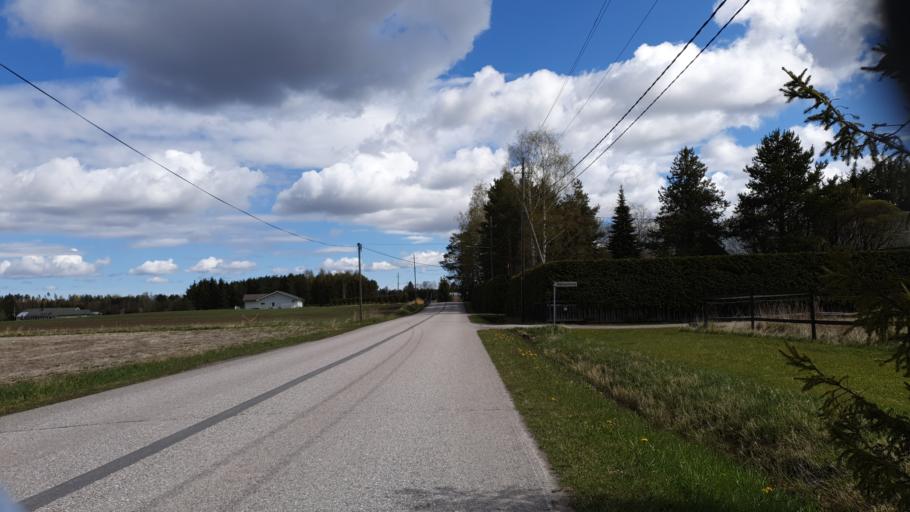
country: FI
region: Uusimaa
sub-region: Helsinki
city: Tuusula
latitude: 60.3927
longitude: 24.9137
